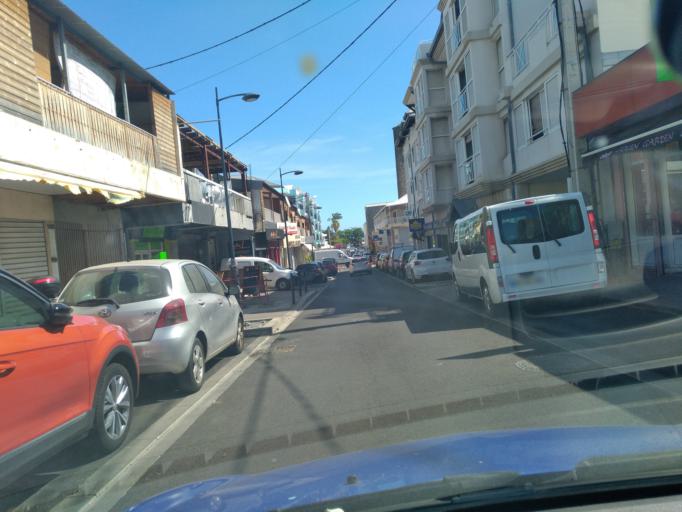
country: RE
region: Reunion
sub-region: Reunion
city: Saint-Pierre
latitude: -21.3414
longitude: 55.4738
